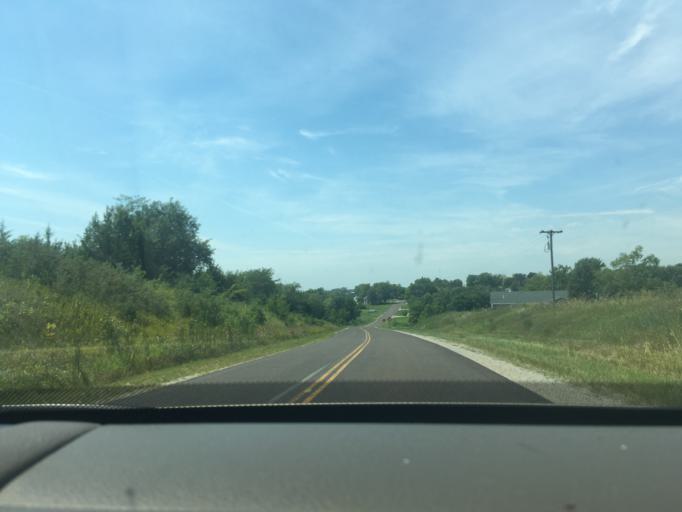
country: US
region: Missouri
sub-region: Nodaway County
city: Maryville
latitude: 40.1747
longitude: -94.8153
